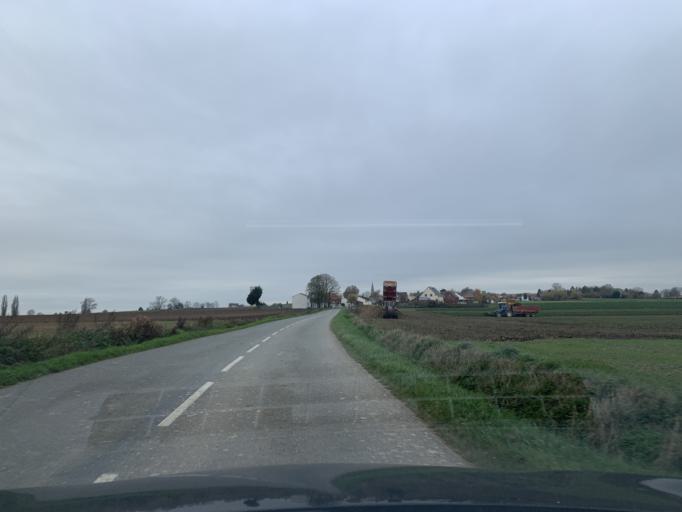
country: FR
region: Nord-Pas-de-Calais
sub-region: Departement du Pas-de-Calais
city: Oisy-le-Verger
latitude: 50.2448
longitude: 3.1340
